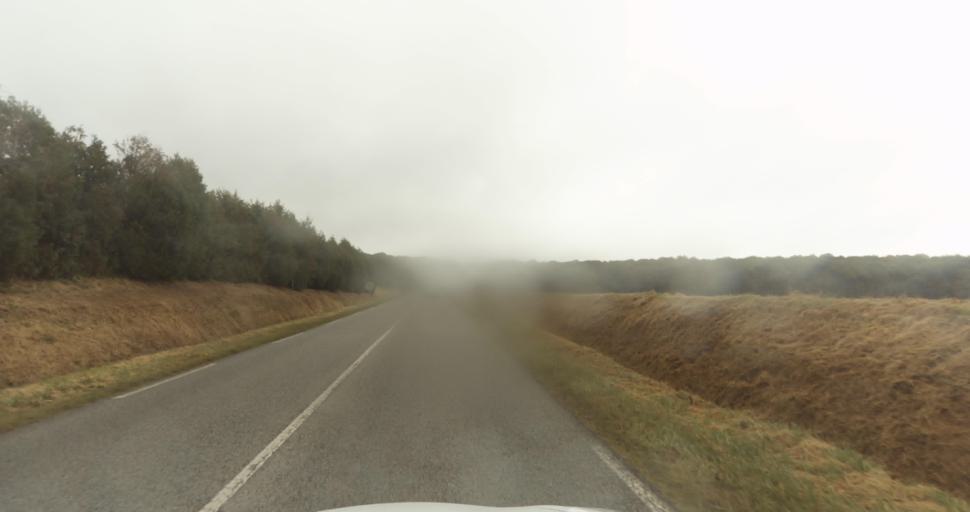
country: FR
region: Haute-Normandie
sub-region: Departement de l'Eure
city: Normanville
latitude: 49.1099
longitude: 1.1730
